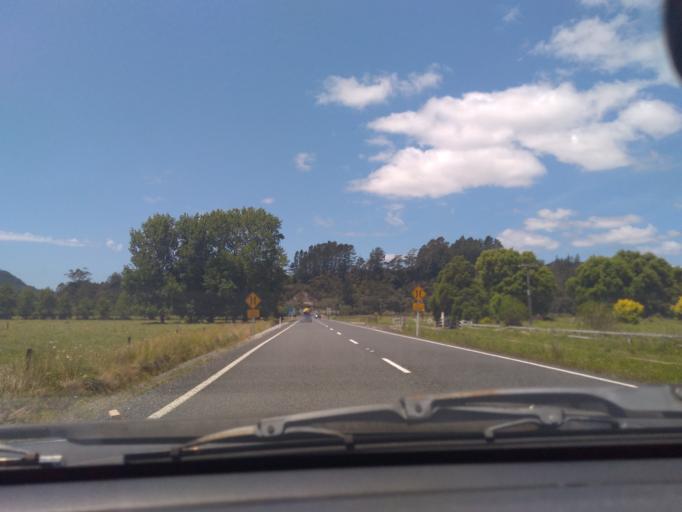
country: NZ
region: Northland
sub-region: Far North District
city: Kerikeri
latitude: -35.0833
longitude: 173.7570
